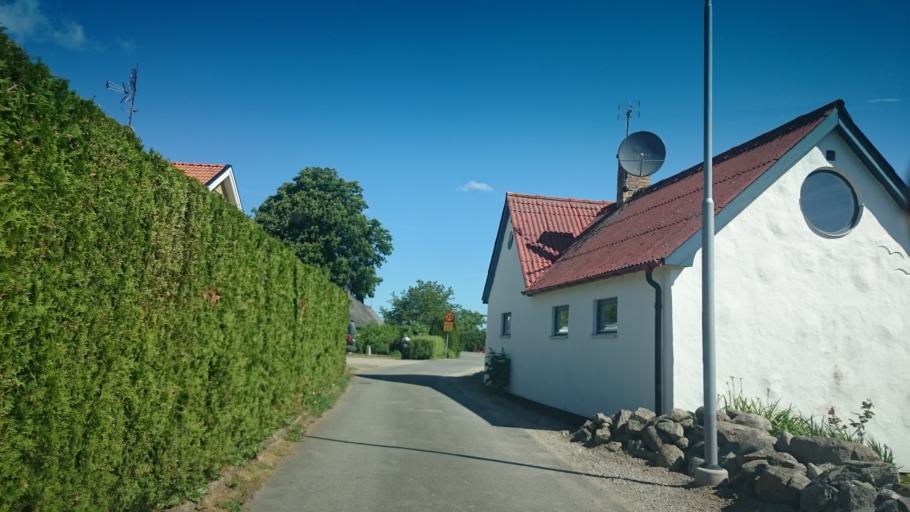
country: SE
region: Blekinge
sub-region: Solvesborgs Kommun
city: Soelvesborg
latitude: 56.0429
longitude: 14.5199
